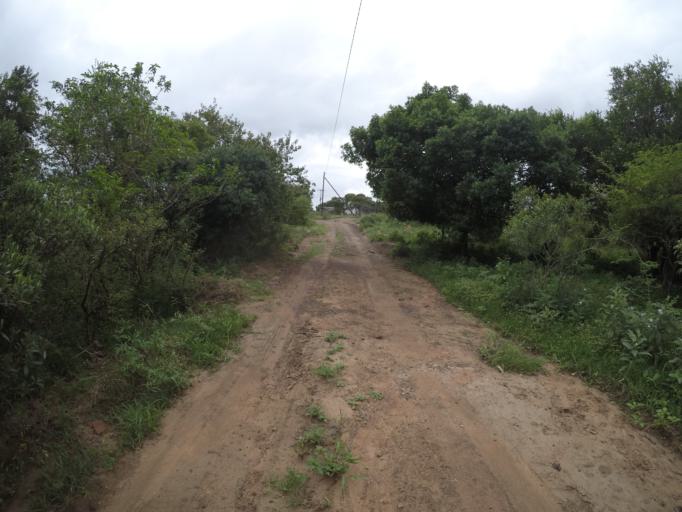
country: ZA
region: KwaZulu-Natal
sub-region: uThungulu District Municipality
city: Empangeni
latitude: -28.6036
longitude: 31.8281
